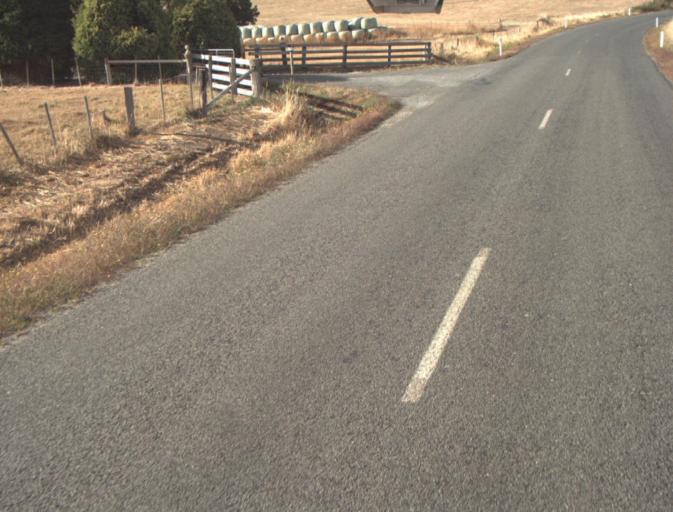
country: AU
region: Tasmania
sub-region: Launceston
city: Mayfield
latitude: -41.1945
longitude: 147.2208
